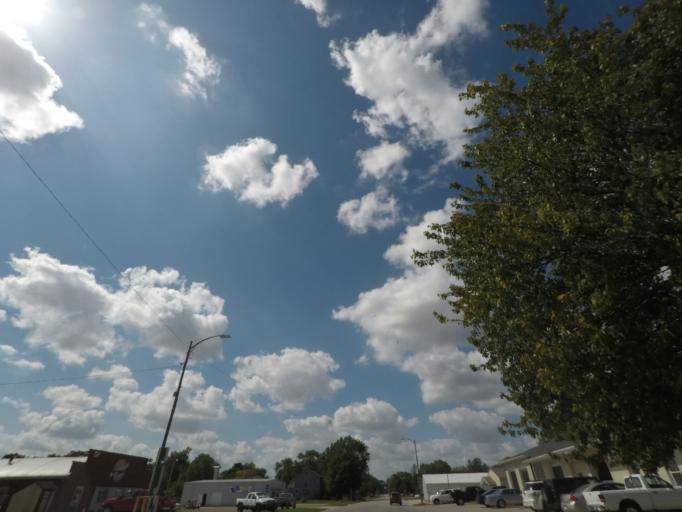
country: US
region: Iowa
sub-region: Story County
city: Nevada
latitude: 42.0228
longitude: -93.4406
